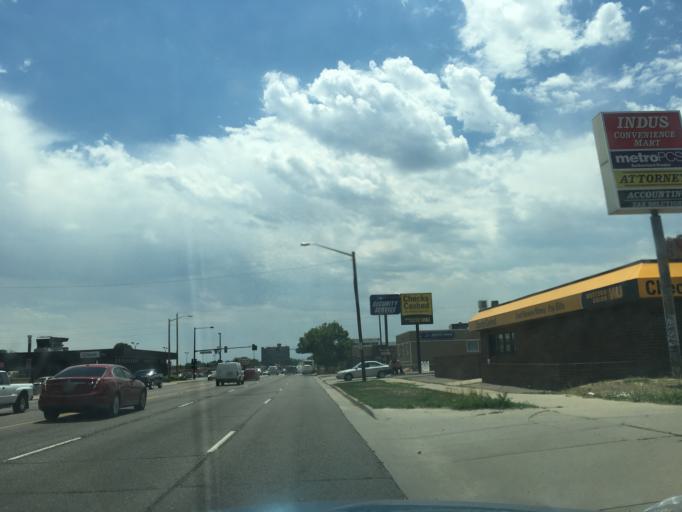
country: US
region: Colorado
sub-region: Arapahoe County
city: Sheridan
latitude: 39.6945
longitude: -105.0252
